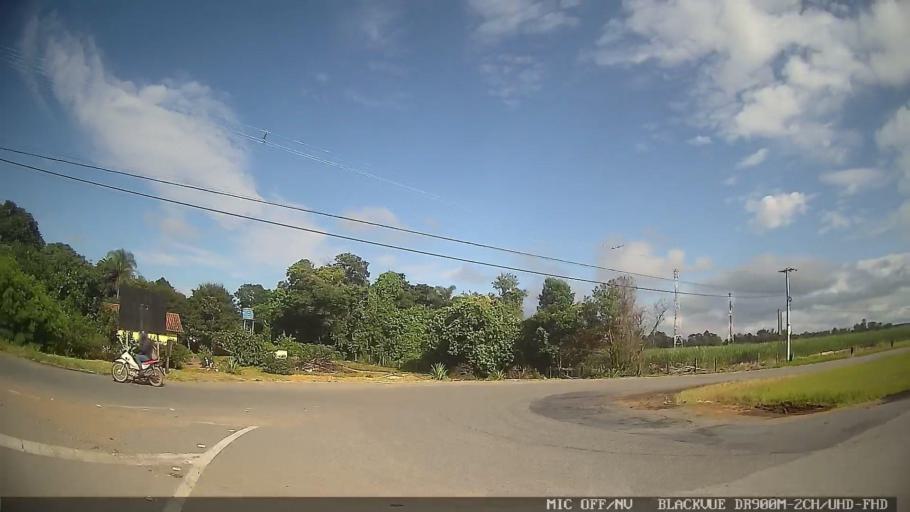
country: BR
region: Sao Paulo
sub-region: Jarinu
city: Jarinu
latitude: -23.0525
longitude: -46.6775
